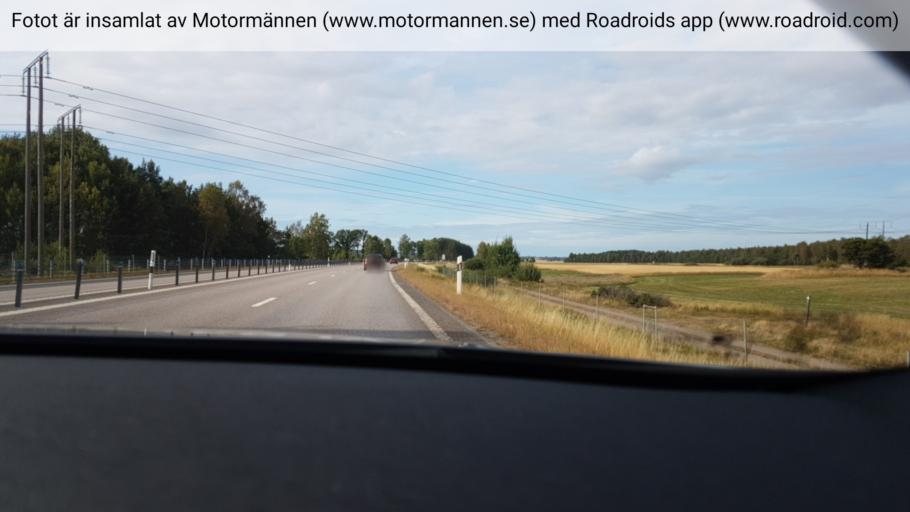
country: SE
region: Vaestra Goetaland
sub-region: Skovde Kommun
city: Stopen
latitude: 58.5683
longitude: 13.7990
